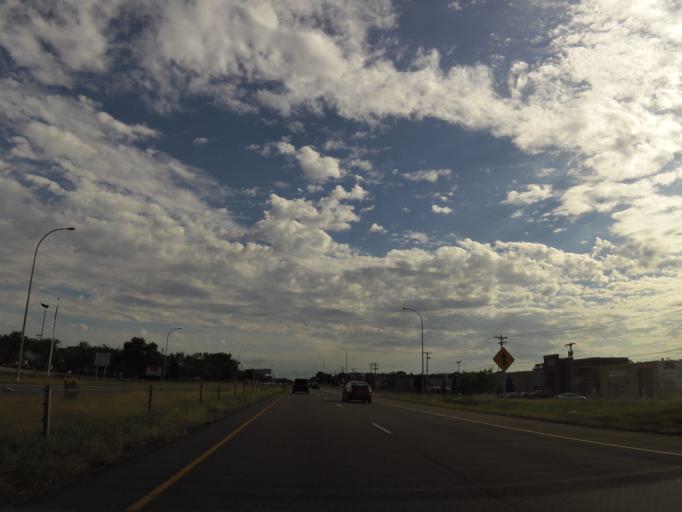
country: US
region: Minnesota
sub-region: Hennepin County
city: New Hope
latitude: 45.0560
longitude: -93.4010
